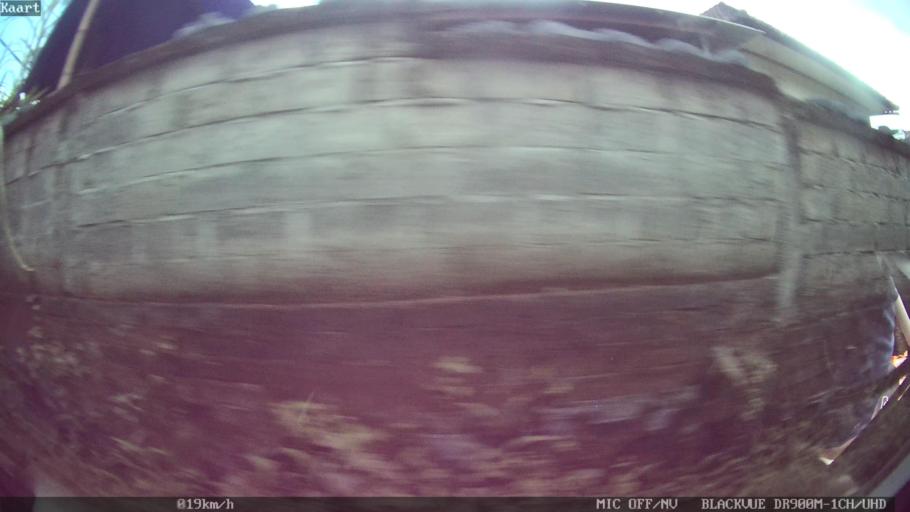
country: ID
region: Bali
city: Banjar Susut Kaja
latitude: -8.4377
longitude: 115.3240
